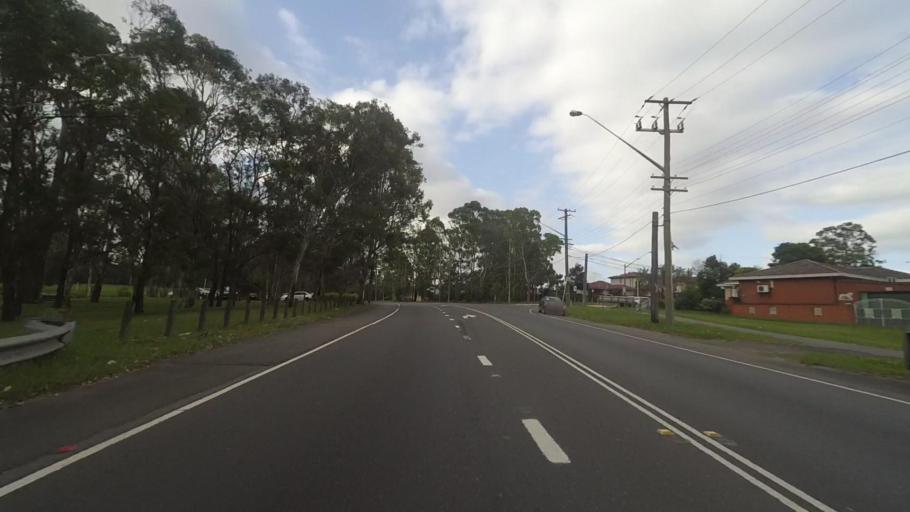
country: AU
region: New South Wales
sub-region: Fairfield
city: Carramar
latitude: -33.9075
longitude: 150.9820
